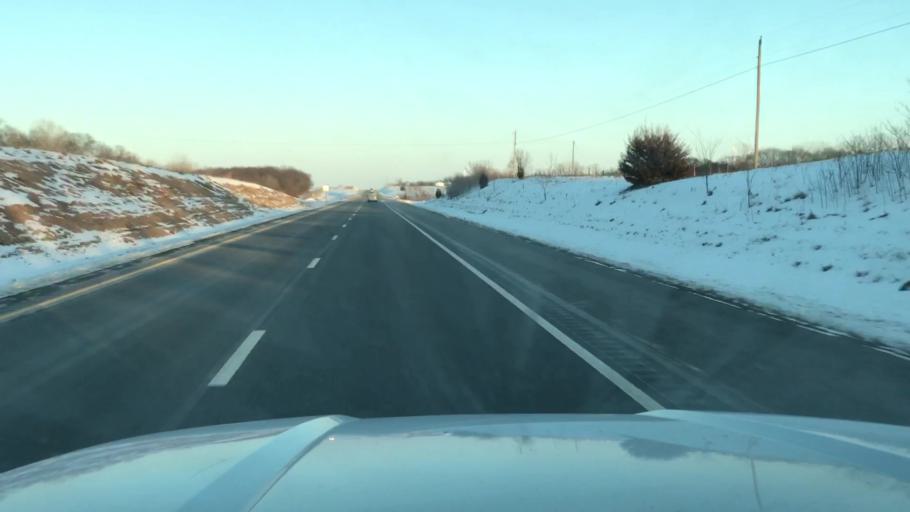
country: US
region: Missouri
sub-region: DeKalb County
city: Maysville
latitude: 39.7620
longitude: -94.4746
